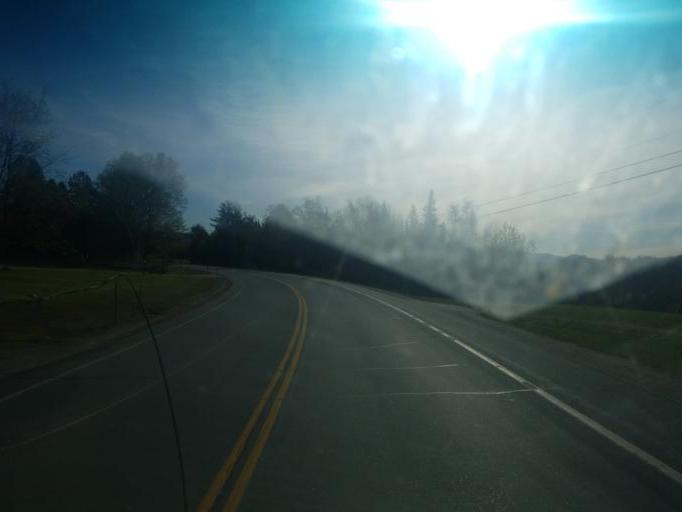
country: US
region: New Hampshire
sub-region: Grafton County
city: Deerfield
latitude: 44.2666
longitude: -71.6180
